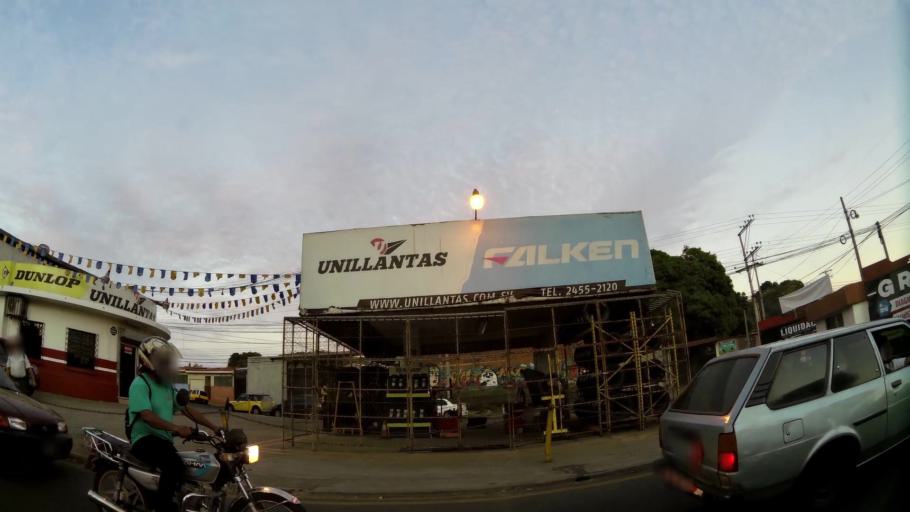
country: SV
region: Santa Ana
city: Santa Ana
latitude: 13.9856
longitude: -89.5476
